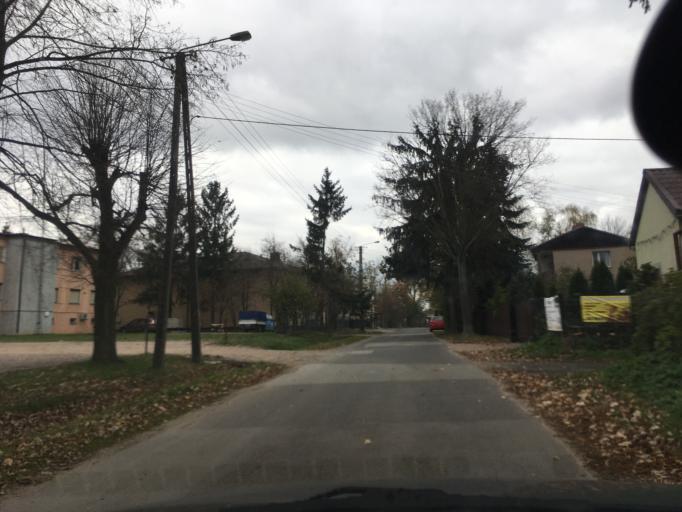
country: PL
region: Lodz Voivodeship
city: Zabia Wola
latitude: 52.0311
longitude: 20.6925
